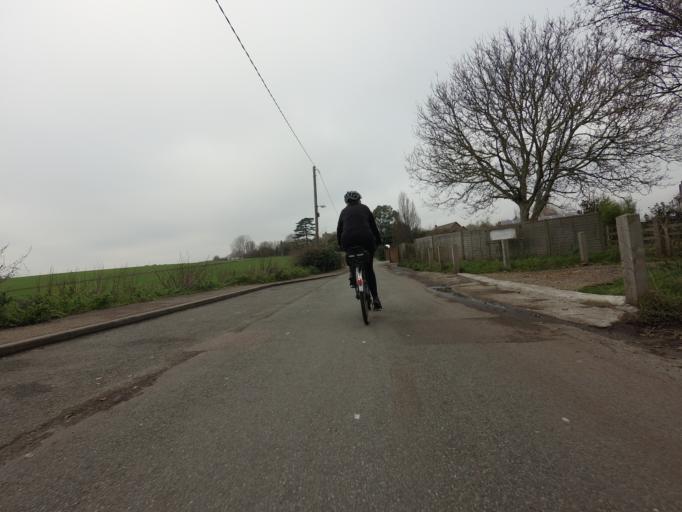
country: GB
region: England
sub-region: Kent
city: Dartford
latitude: 51.4119
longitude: 0.2345
